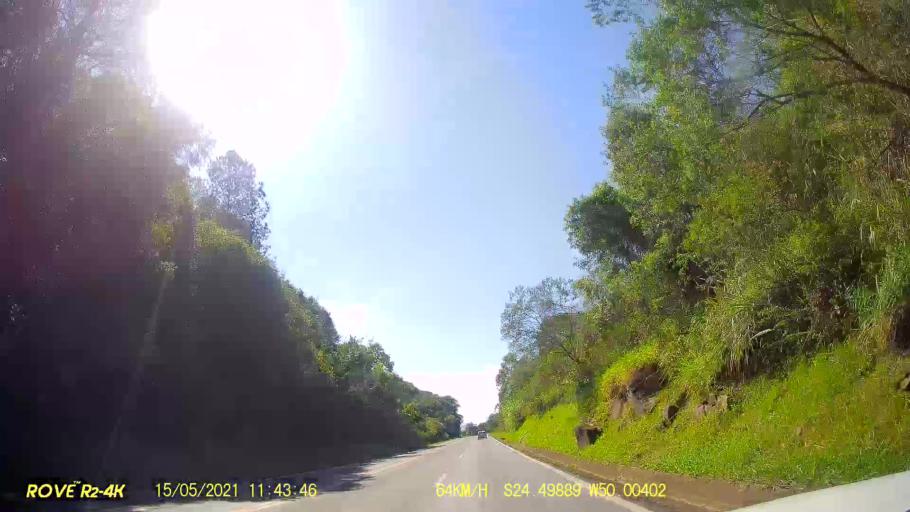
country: BR
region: Parana
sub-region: Pirai Do Sul
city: Pirai do Sul
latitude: -24.4989
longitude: -50.0040
